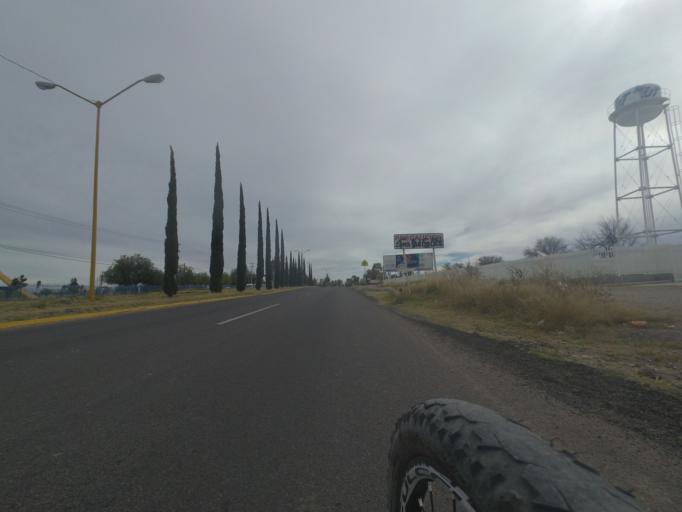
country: MX
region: Aguascalientes
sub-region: Aguascalientes
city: La Loma de los Negritos
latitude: 21.8428
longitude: -102.3547
